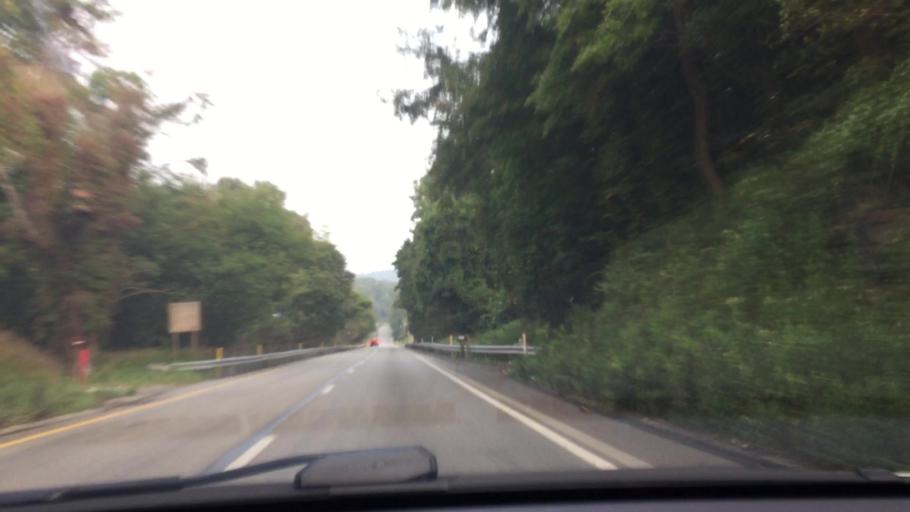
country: US
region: Pennsylvania
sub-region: Westmoreland County
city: Fellsburg
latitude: 40.1962
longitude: -79.8286
